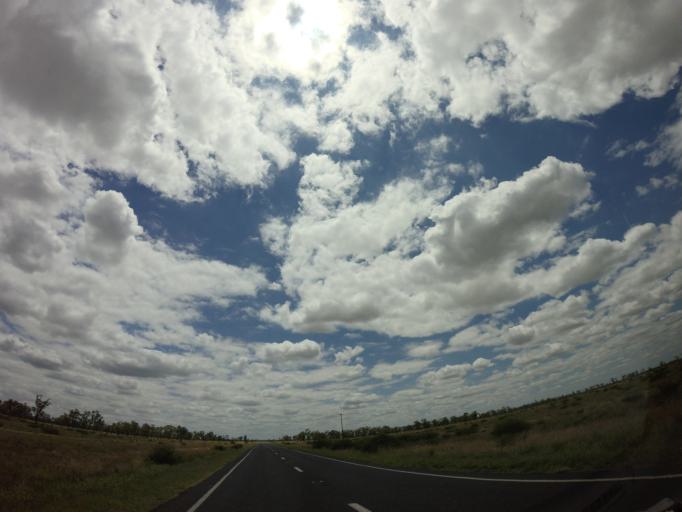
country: AU
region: New South Wales
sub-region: Moree Plains
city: Boggabilla
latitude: -28.6640
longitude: 150.3237
